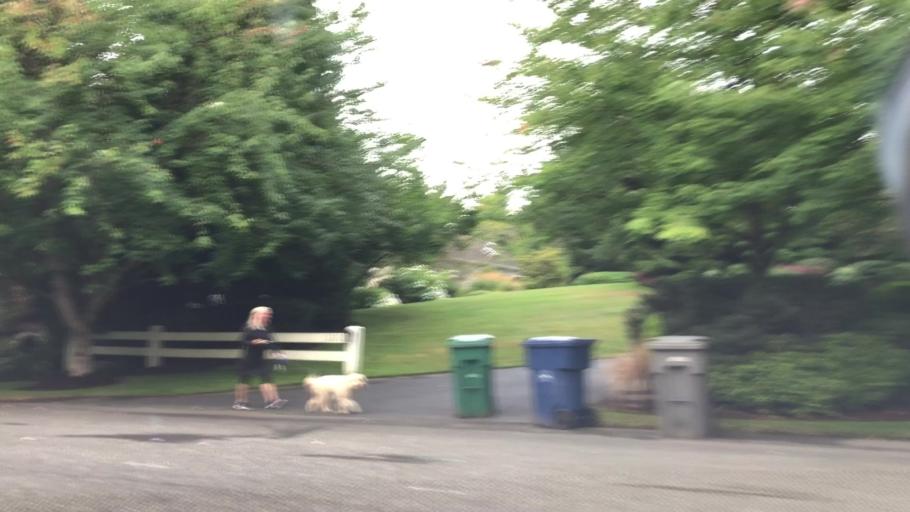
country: US
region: Washington
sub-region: King County
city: Cottage Lake
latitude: 47.7187
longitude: -122.0993
